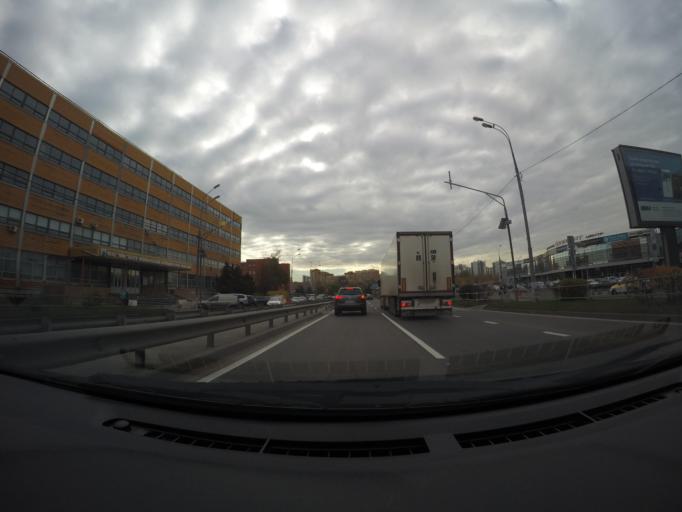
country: RU
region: Moskovskaya
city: Mytishchi
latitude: 55.9306
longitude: 37.7525
